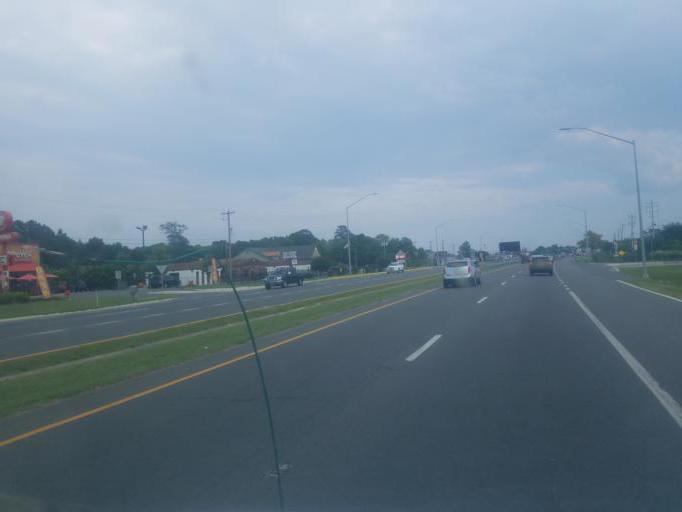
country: US
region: Maryland
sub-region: Worcester County
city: West Ocean City
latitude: 38.3390
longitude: -75.1172
